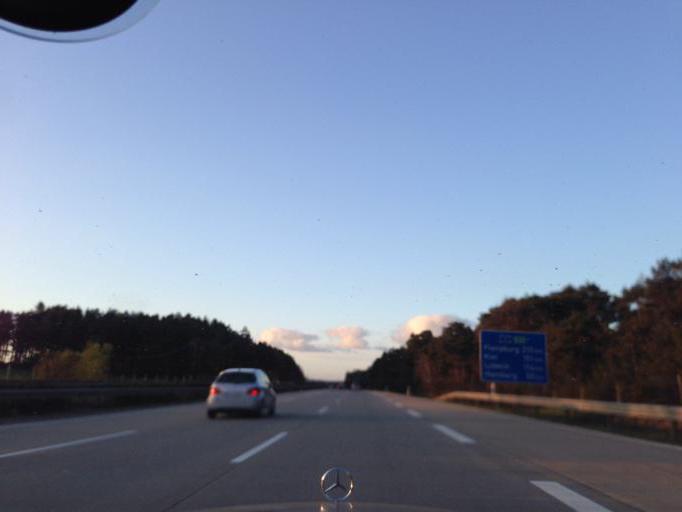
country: DE
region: Lower Saxony
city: Bispingen
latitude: 53.1148
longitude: 9.9861
